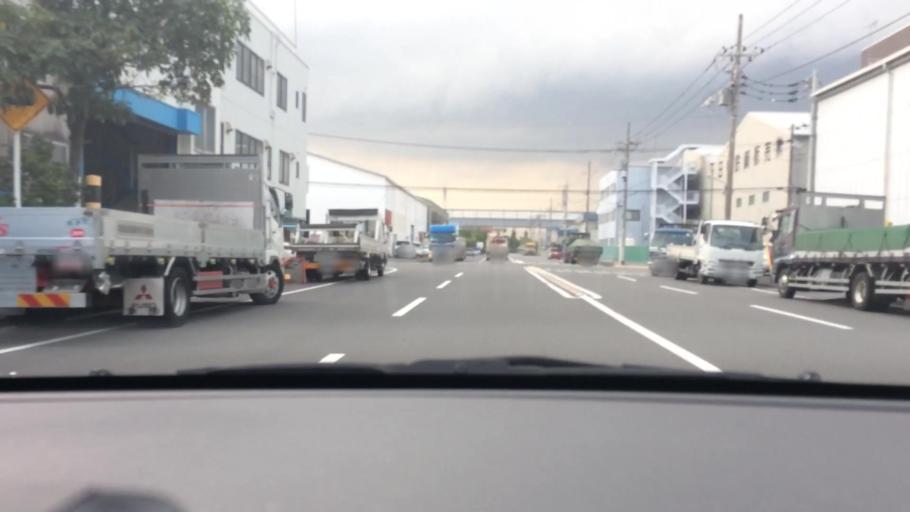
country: JP
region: Tokyo
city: Urayasu
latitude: 35.6357
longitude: 139.9003
